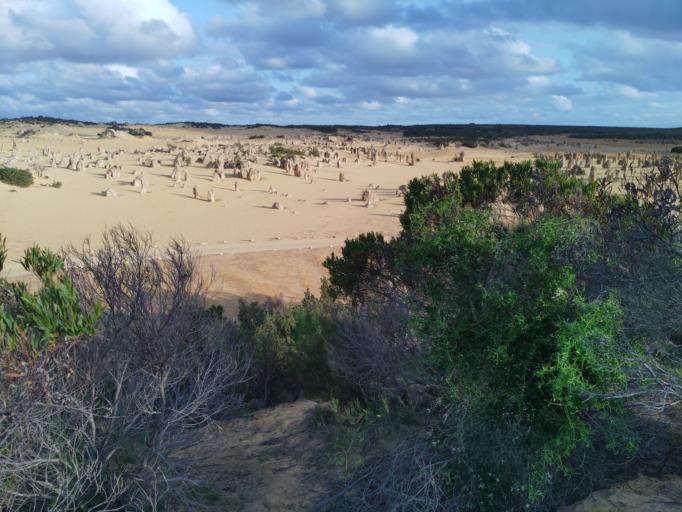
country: AU
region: Western Australia
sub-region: Dandaragan
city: Jurien Bay
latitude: -30.6128
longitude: 115.1388
